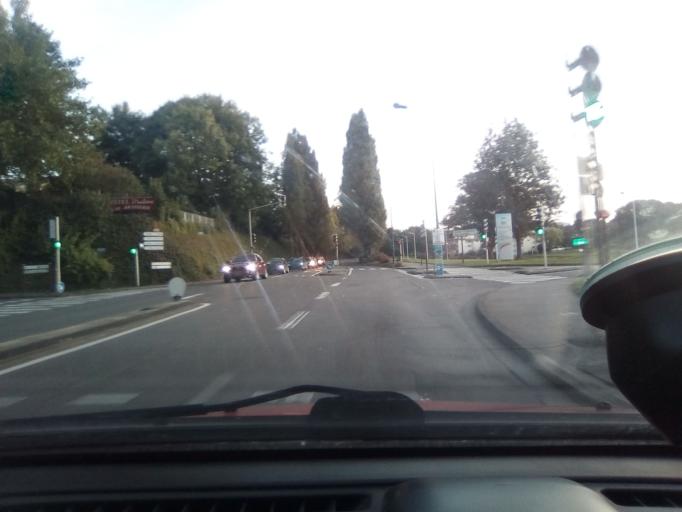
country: FR
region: Lower Normandy
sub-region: Departement du Calvados
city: Vire
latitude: 48.8457
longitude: -0.8864
